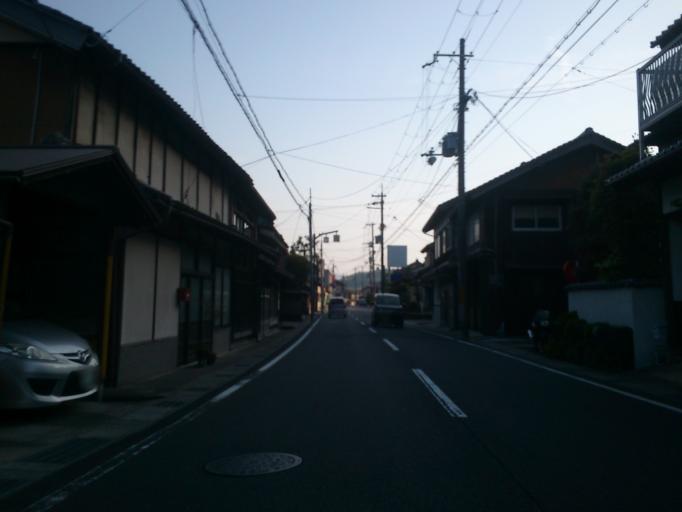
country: JP
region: Kyoto
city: Miyazu
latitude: 35.5646
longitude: 135.1488
